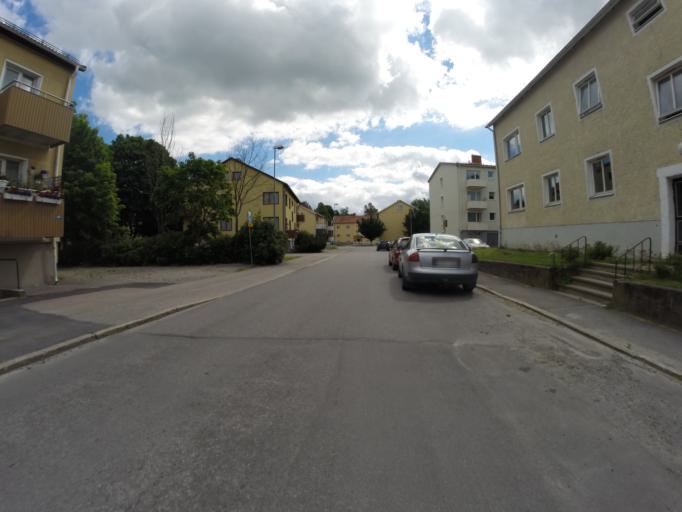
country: SE
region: Soedermanland
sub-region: Eskilstuna Kommun
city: Torshalla
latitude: 59.4212
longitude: 16.4771
